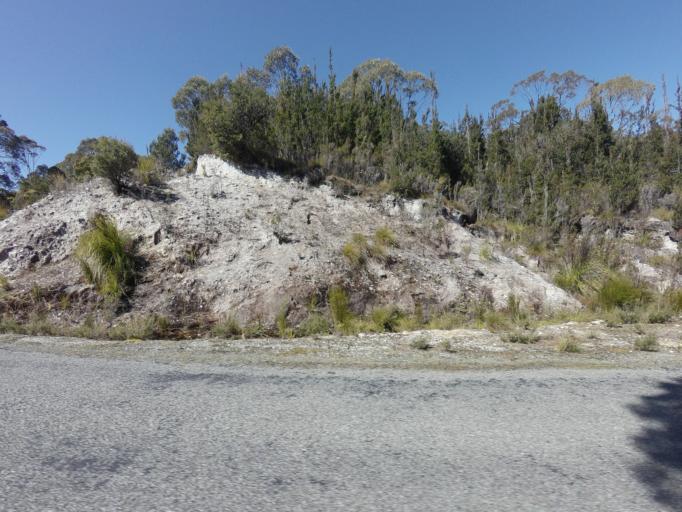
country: AU
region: Tasmania
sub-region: Derwent Valley
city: New Norfolk
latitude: -42.7627
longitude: 146.3966
